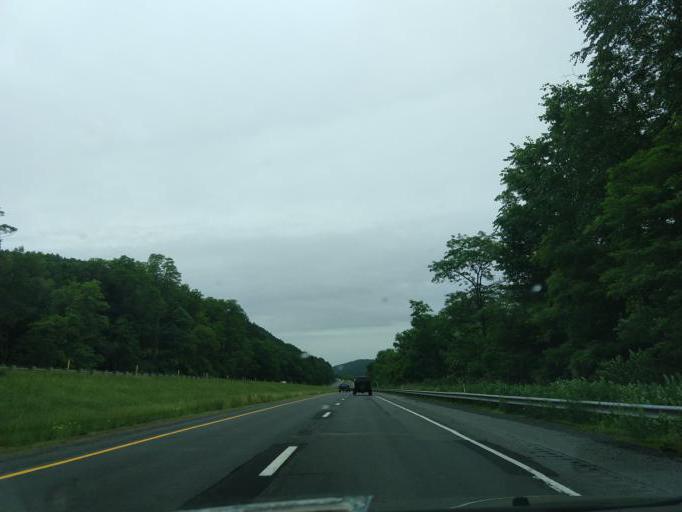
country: US
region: Pennsylvania
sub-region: Susquehanna County
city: Hallstead
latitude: 41.9221
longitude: -75.7309
